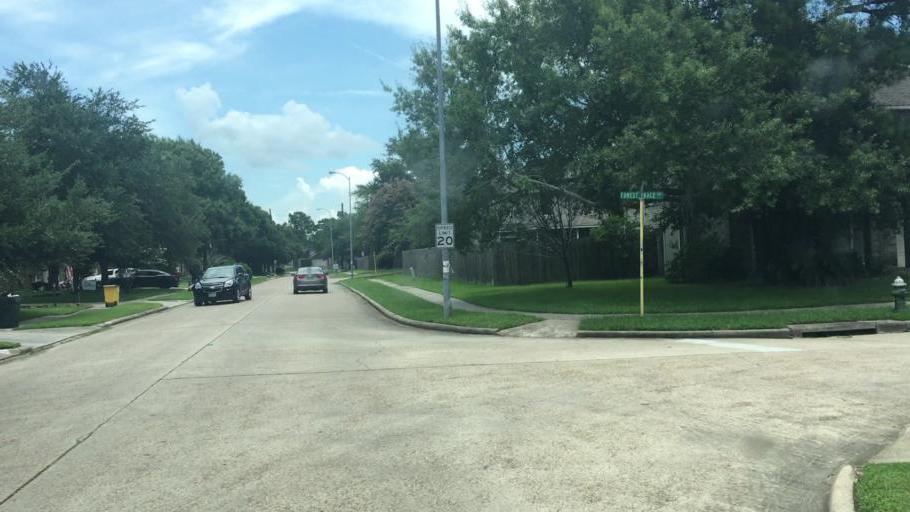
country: US
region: Texas
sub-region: Harris County
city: Atascocita
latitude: 29.9942
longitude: -95.1735
